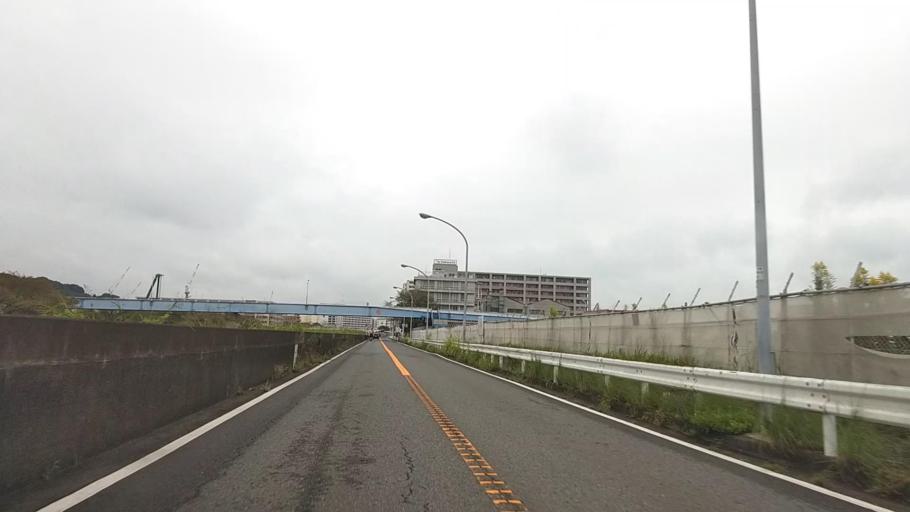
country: JP
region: Kanagawa
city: Fujisawa
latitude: 35.3916
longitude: 139.5332
